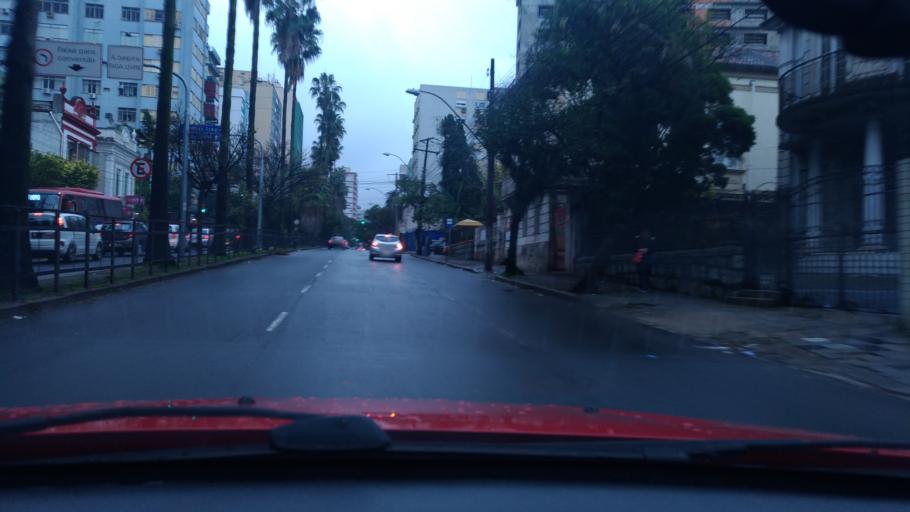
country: BR
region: Rio Grande do Sul
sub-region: Porto Alegre
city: Porto Alegre
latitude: -30.0294
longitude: -51.2115
